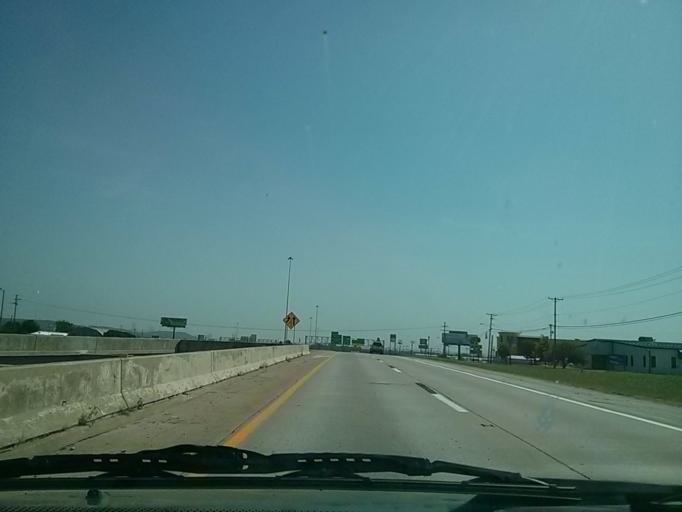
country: US
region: Oklahoma
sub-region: Tulsa County
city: Oakhurst
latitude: 36.0739
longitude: -96.0556
